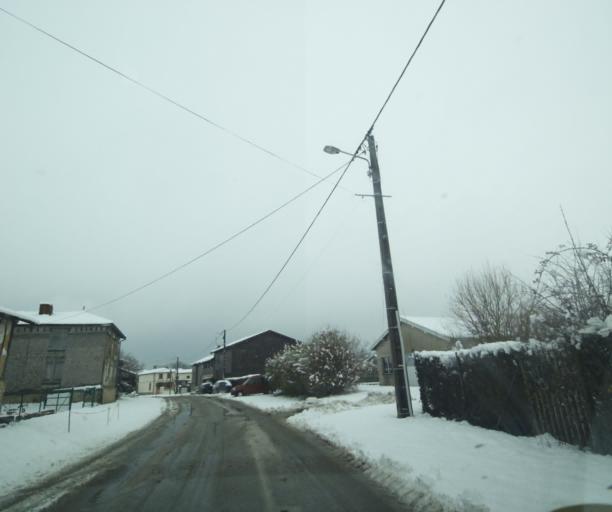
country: FR
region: Champagne-Ardenne
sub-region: Departement de la Haute-Marne
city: Montier-en-Der
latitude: 48.5069
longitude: 4.7843
